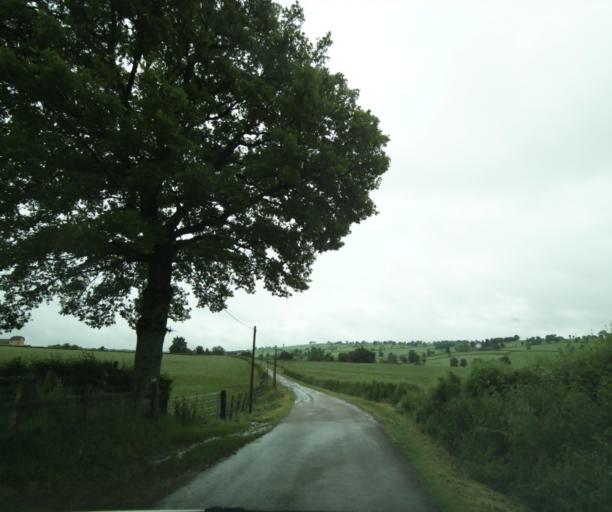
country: FR
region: Bourgogne
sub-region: Departement de Saone-et-Loire
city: Charolles
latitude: 46.3767
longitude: 4.2229
